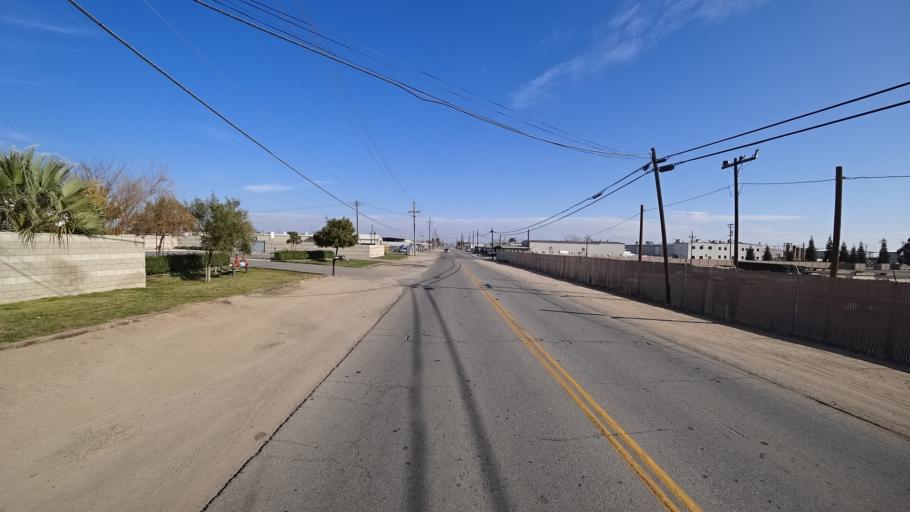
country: US
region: California
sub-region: Kern County
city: Greenacres
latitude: 35.3905
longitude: -119.0842
